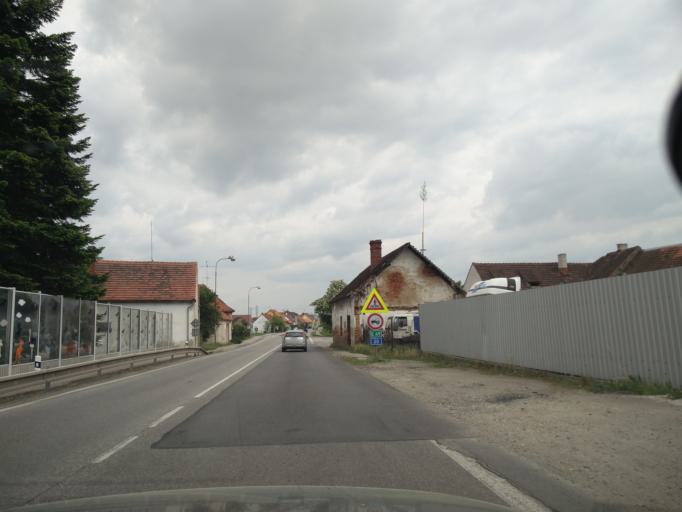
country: CZ
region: Jihocesky
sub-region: Okres Ceske Budejovice
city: Hluboka nad Vltavou
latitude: 49.0192
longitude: 14.4065
